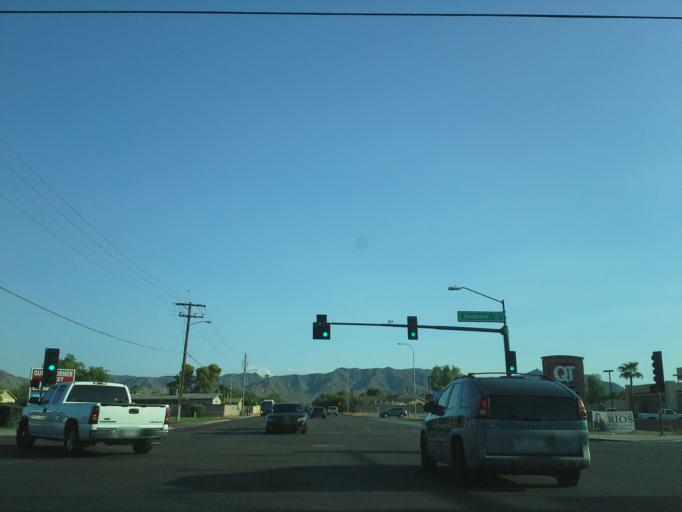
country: US
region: Arizona
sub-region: Maricopa County
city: Phoenix
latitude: 33.3924
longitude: -112.0992
